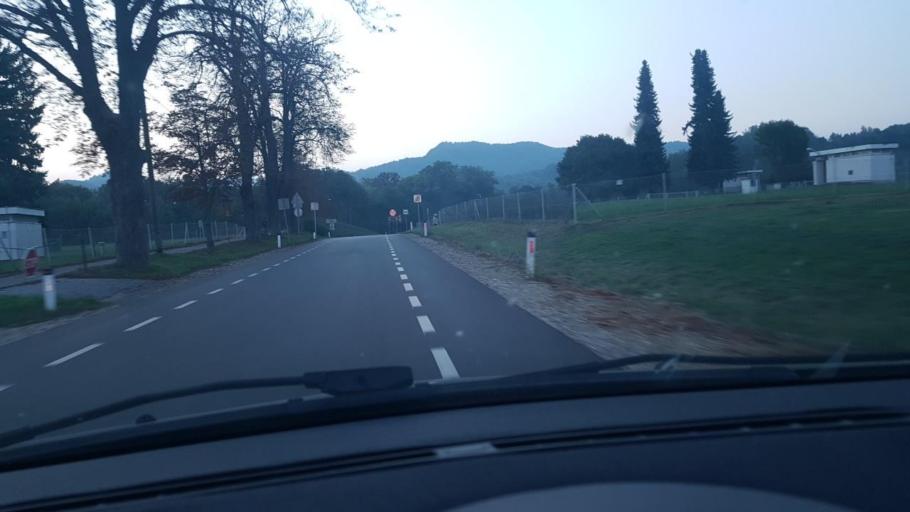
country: SI
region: Maribor
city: Kamnica
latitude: 46.5697
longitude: 15.6283
